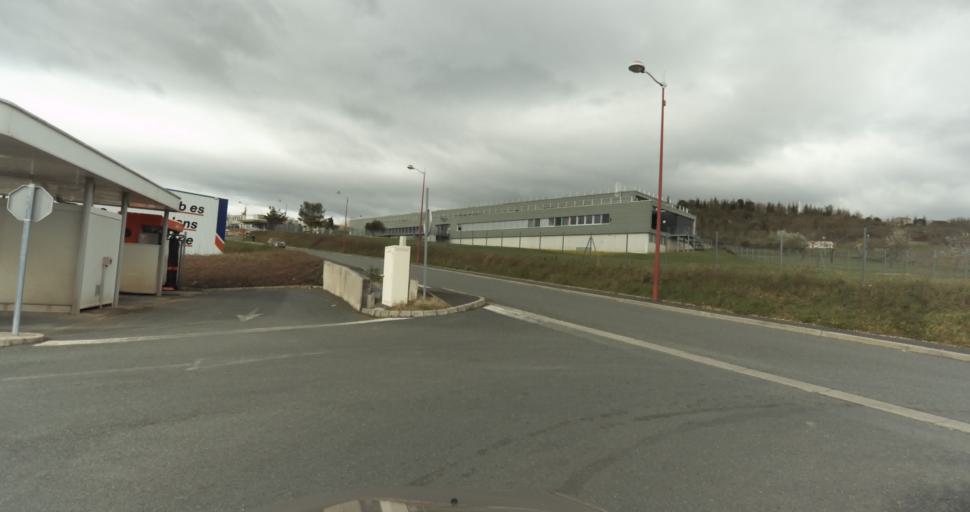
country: FR
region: Midi-Pyrenees
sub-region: Departement du Tarn
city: Puygouzon
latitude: 43.8926
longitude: 2.1653
